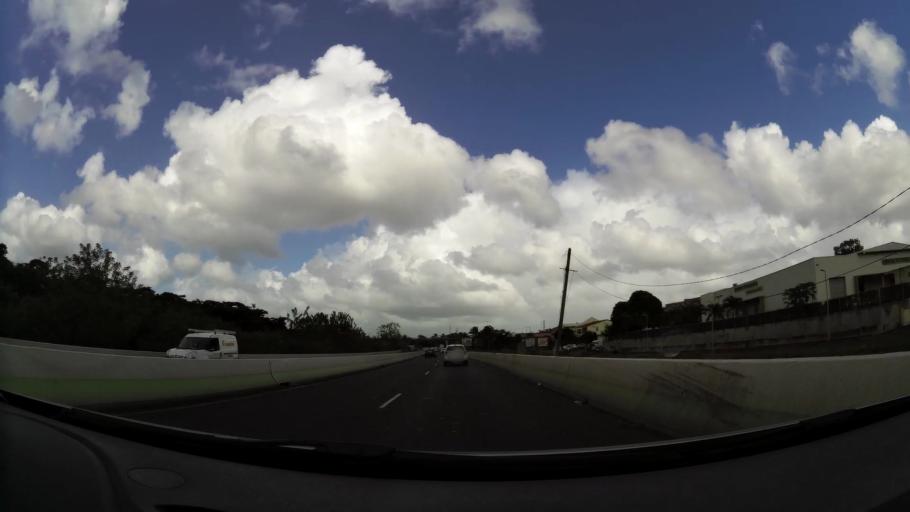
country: MQ
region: Martinique
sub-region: Martinique
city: Ducos
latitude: 14.5276
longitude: -60.9823
